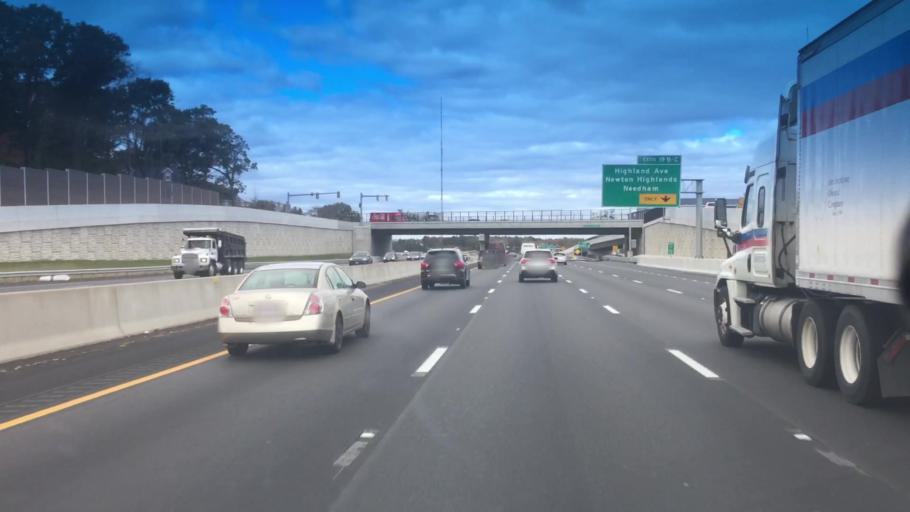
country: US
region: Massachusetts
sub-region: Norfolk County
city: Needham
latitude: 42.2939
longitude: -71.2166
